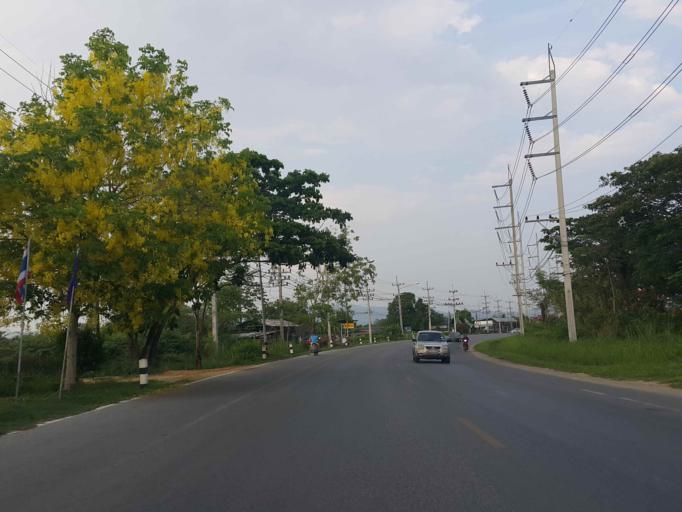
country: TH
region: Chiang Mai
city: San Sai
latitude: 18.9160
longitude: 98.9610
